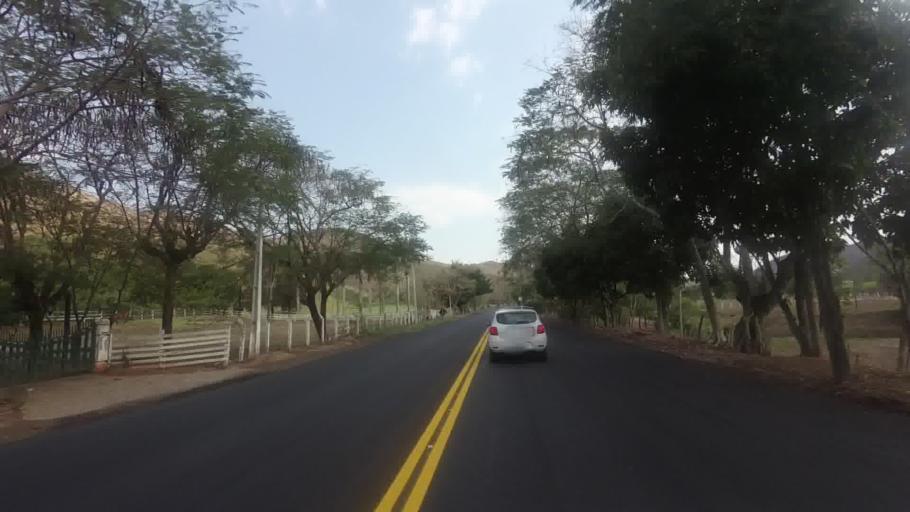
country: BR
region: Rio de Janeiro
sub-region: Bom Jesus Do Itabapoana
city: Bom Jesus do Itabapoana
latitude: -21.2191
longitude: -41.7384
